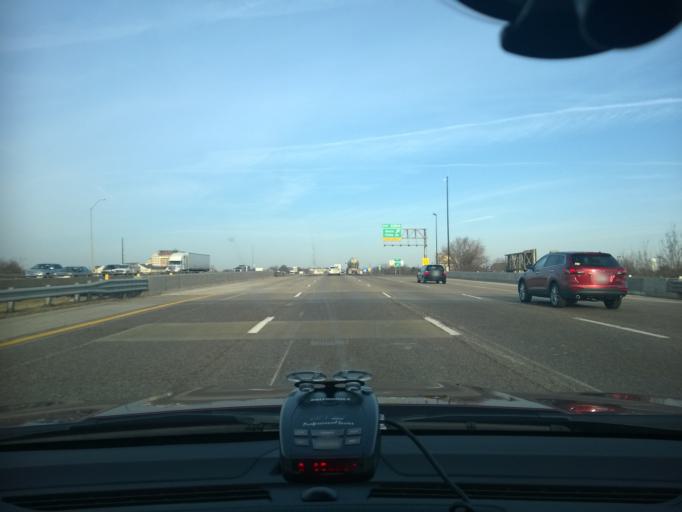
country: US
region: Missouri
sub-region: Saint Charles County
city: Saint Charles
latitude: 38.7690
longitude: -90.4949
